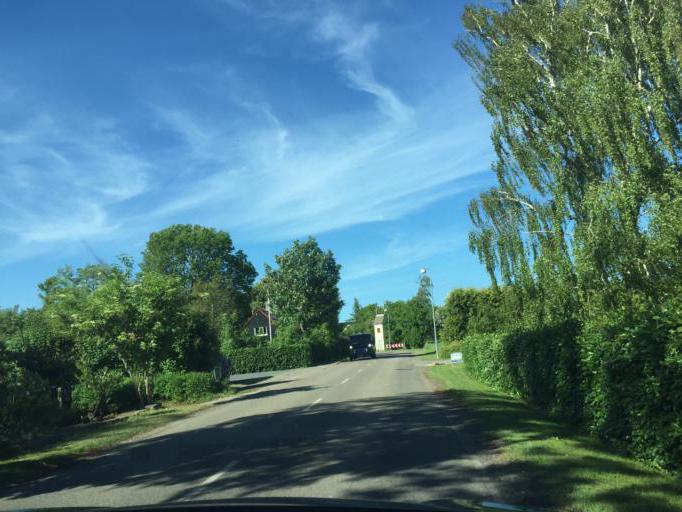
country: DK
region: Zealand
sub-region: Stevns Kommune
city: Harlev
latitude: 55.3627
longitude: 12.1909
